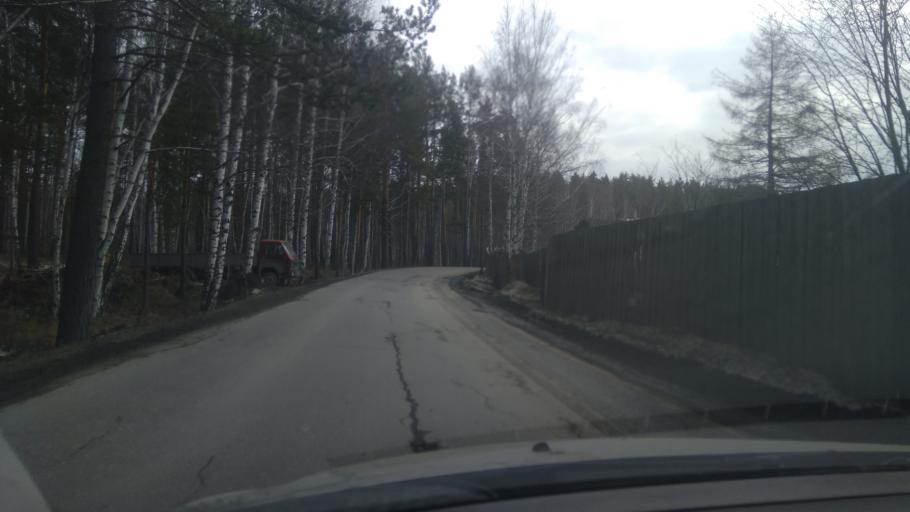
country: RU
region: Sverdlovsk
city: Severka
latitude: 56.8424
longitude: 60.3850
